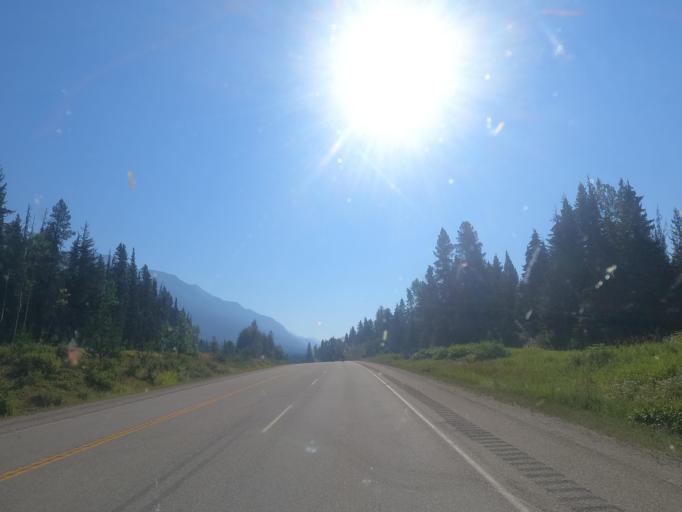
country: CA
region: Alberta
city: Grande Cache
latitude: 53.0038
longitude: -119.0491
